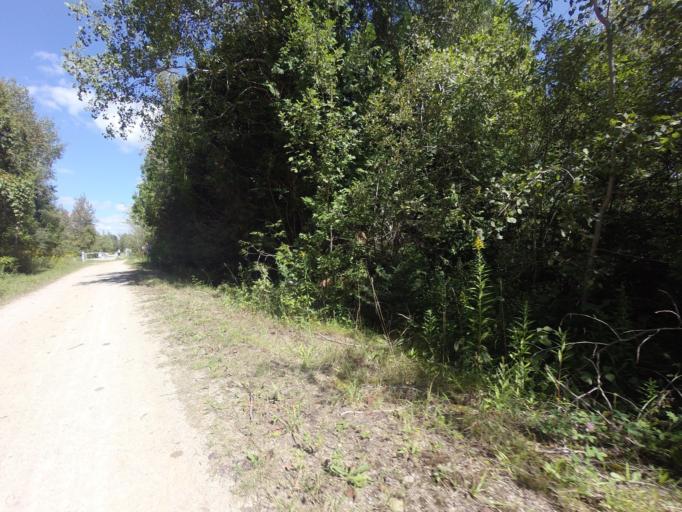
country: CA
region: Ontario
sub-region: Wellington County
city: Guelph
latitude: 43.7460
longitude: -80.3169
